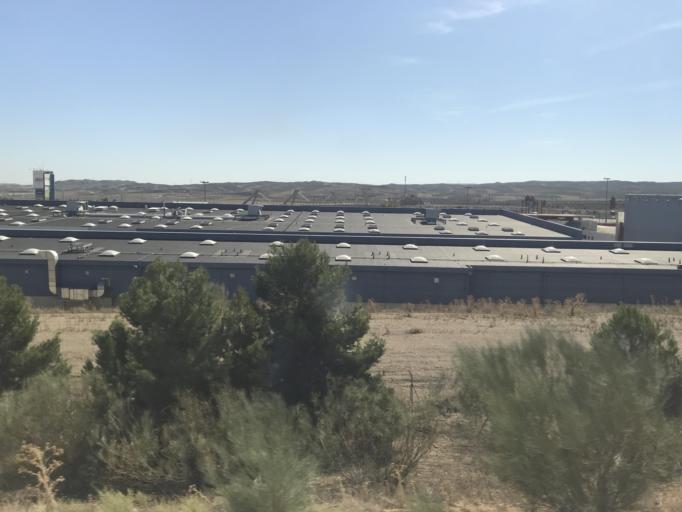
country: ES
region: Aragon
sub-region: Provincia de Zaragoza
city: Montecanal
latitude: 41.6332
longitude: -0.9925
